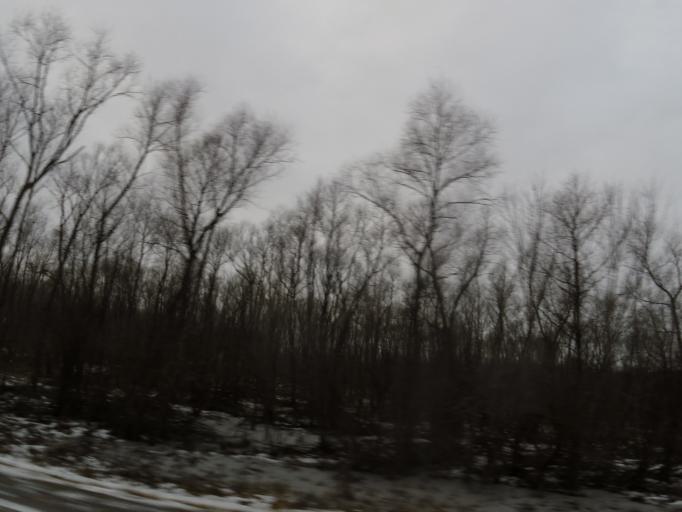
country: US
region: Minnesota
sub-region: Scott County
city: Jordan
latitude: 44.6991
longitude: -93.6438
